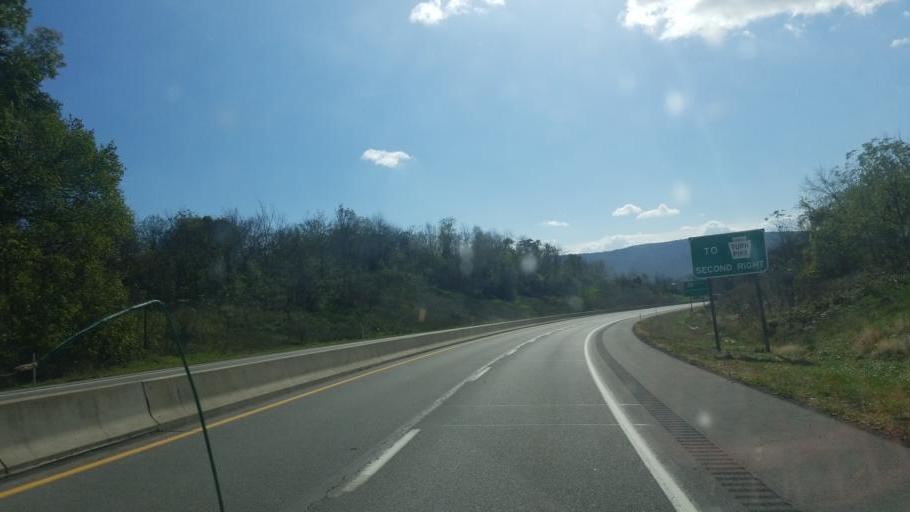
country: US
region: Pennsylvania
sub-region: Bedford County
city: Bedford
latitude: 40.0342
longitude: -78.5184
